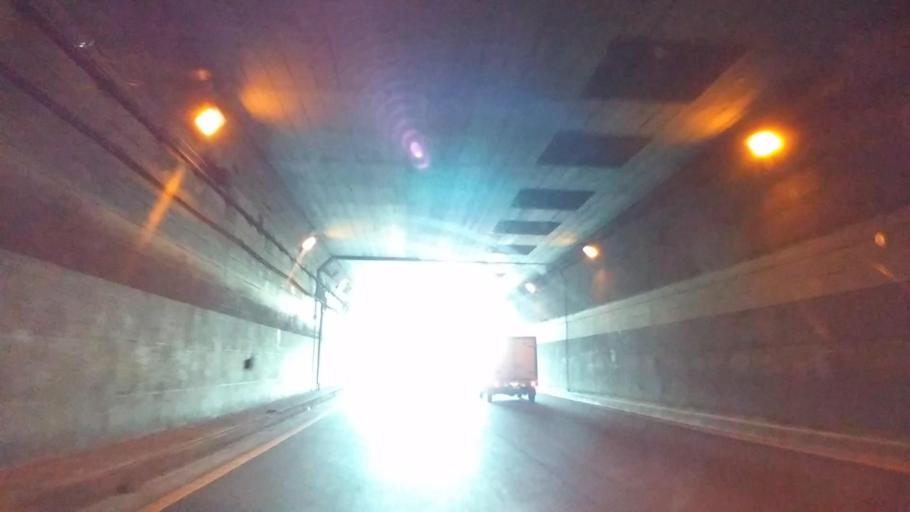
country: JP
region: Kanagawa
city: Minami-rinkan
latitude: 35.4867
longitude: 139.4612
